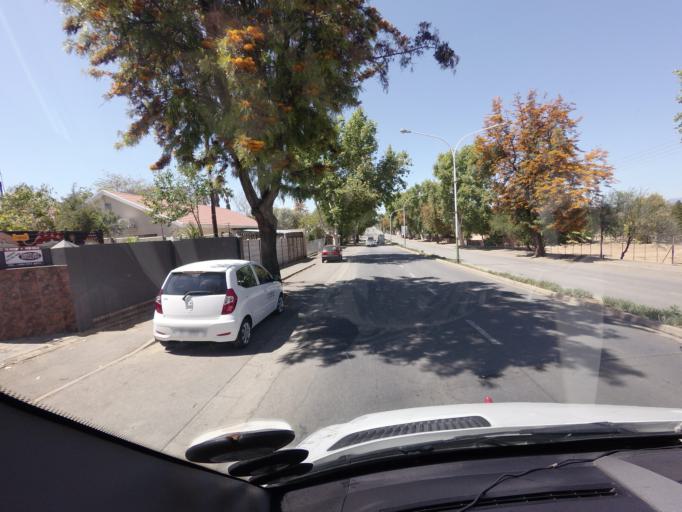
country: ZA
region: Western Cape
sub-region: Eden District Municipality
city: Oudtshoorn
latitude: -33.6056
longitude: 22.2105
